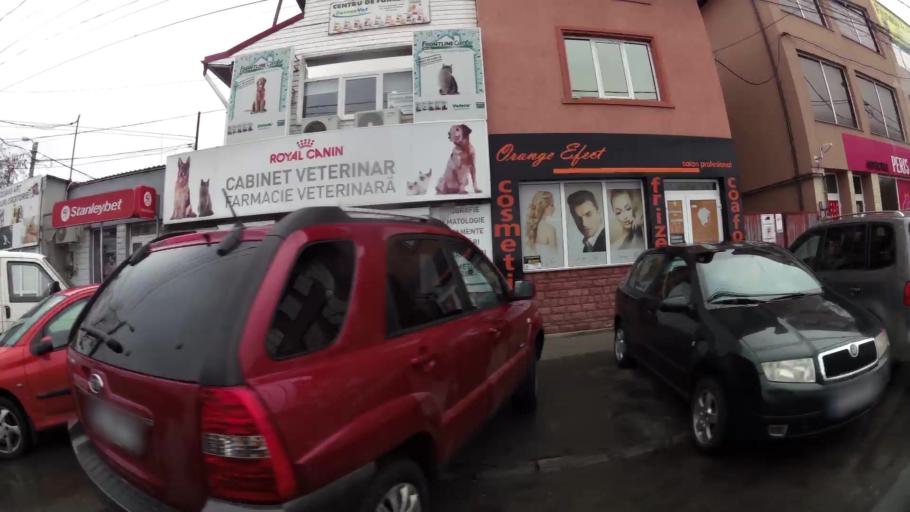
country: RO
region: Ilfov
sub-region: Comuna Chiajna
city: Rosu
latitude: 44.4851
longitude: 26.0321
